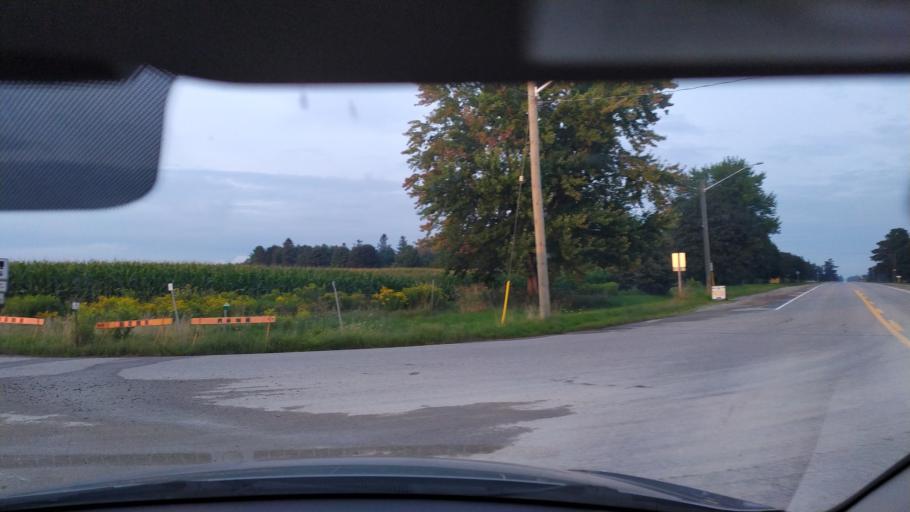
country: CA
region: Ontario
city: Kitchener
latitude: 43.3052
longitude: -80.6095
